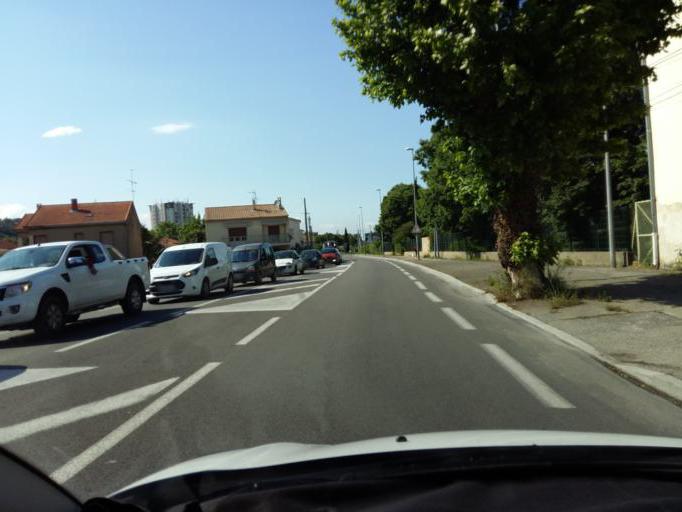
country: FR
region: Provence-Alpes-Cote d'Azur
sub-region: Departement du Vaucluse
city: Cavaillon
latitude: 43.8421
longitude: 5.0459
